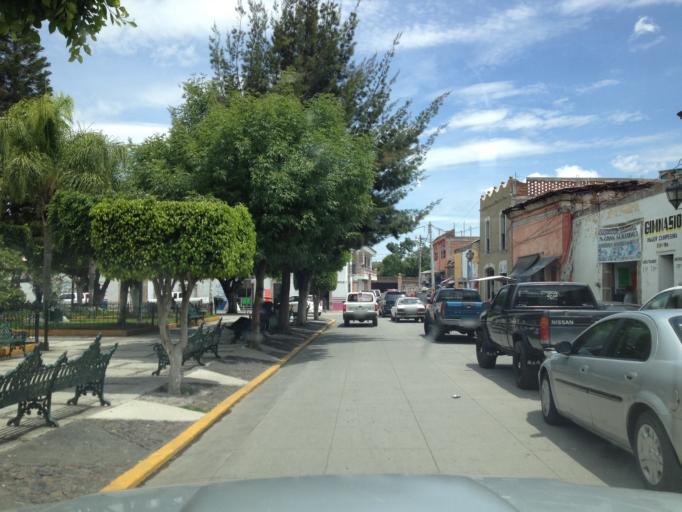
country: MX
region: Michoacan
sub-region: Tarimbaro
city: Meson Nuevo (Canada de la Magdalena)
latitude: 19.7954
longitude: -101.1765
